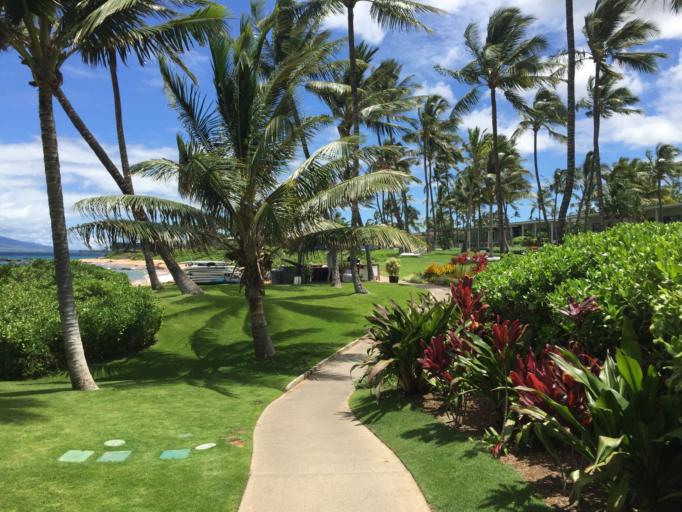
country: US
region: Hawaii
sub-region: Maui County
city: Kihei
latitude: 20.6920
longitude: -156.4439
